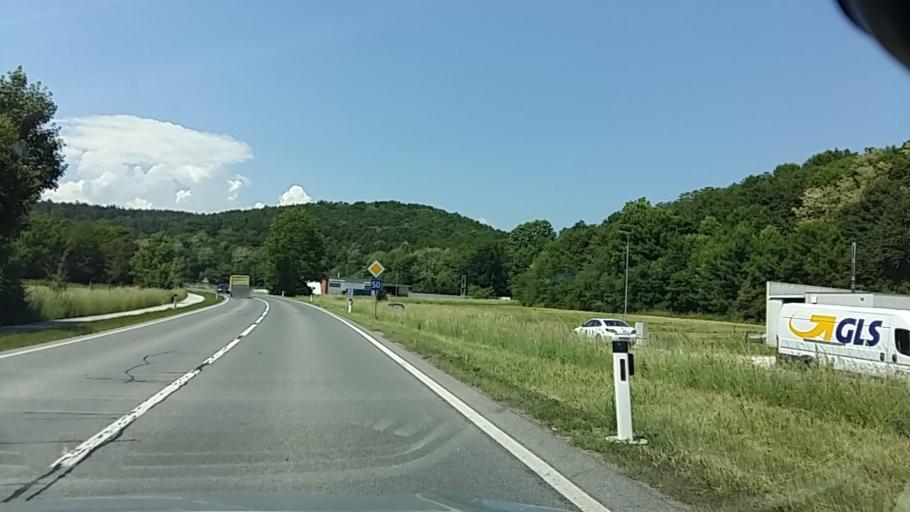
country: AT
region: Burgenland
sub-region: Politischer Bezirk Oberpullendorf
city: Oberpullendorf
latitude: 47.4857
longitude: 16.4716
